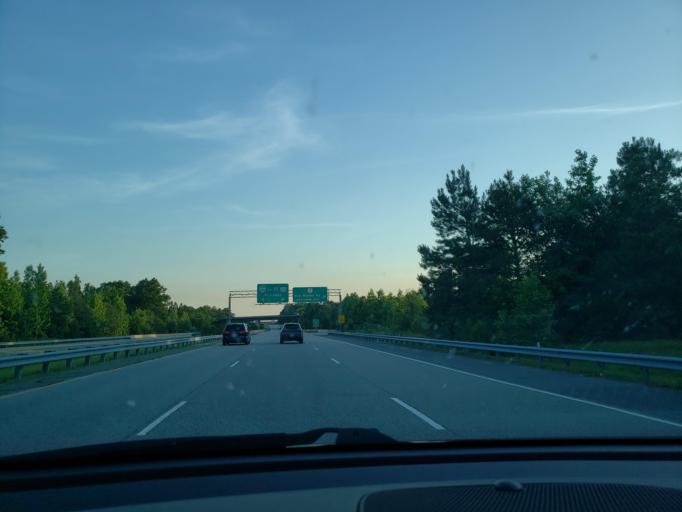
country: US
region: Virginia
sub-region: Henrico County
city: Fort Lee
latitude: 37.4603
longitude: -77.3813
